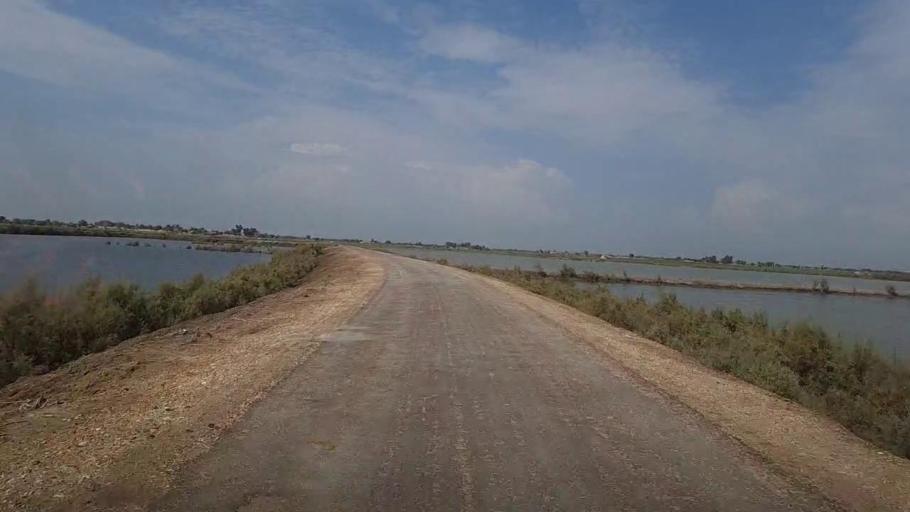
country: PK
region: Sindh
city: Thul
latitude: 28.2832
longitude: 68.8231
